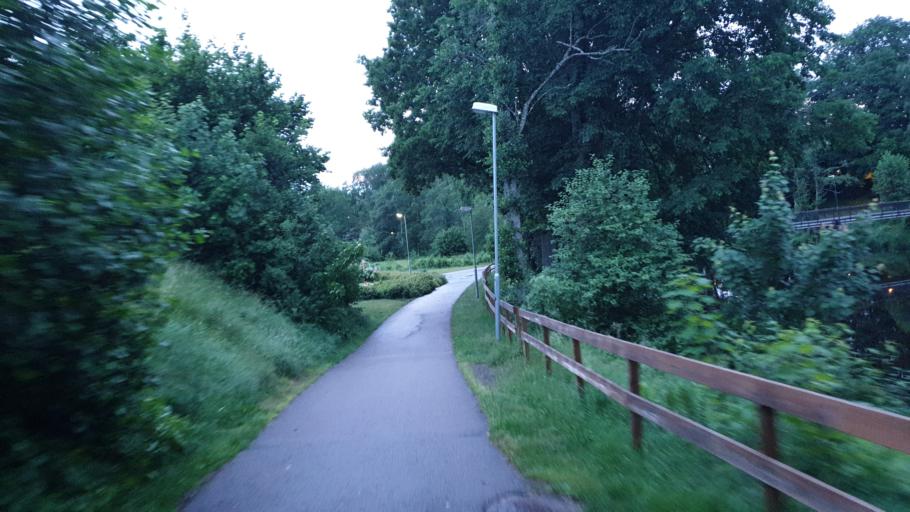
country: SE
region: Kronoberg
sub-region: Ljungby Kommun
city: Ljungby
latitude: 56.8285
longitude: 13.9424
